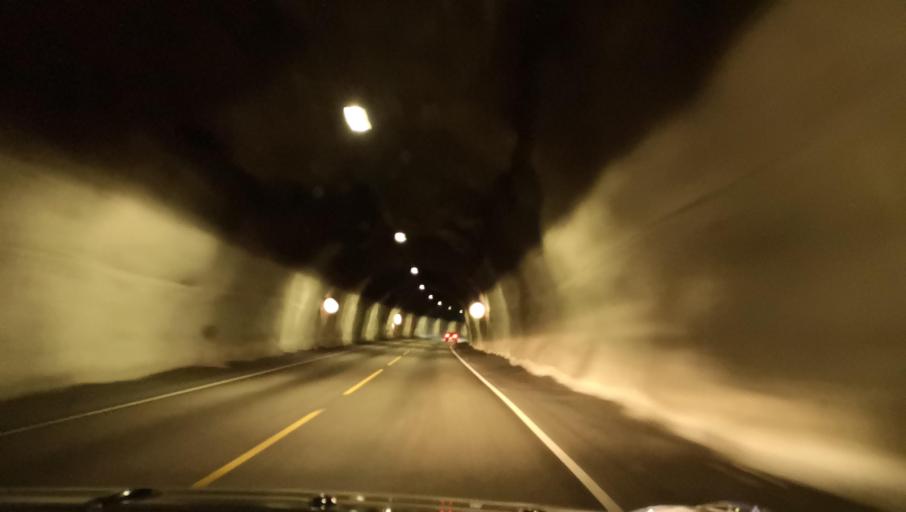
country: NO
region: Hordaland
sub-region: Granvin
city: Granvin
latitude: 60.5320
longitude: 6.7393
